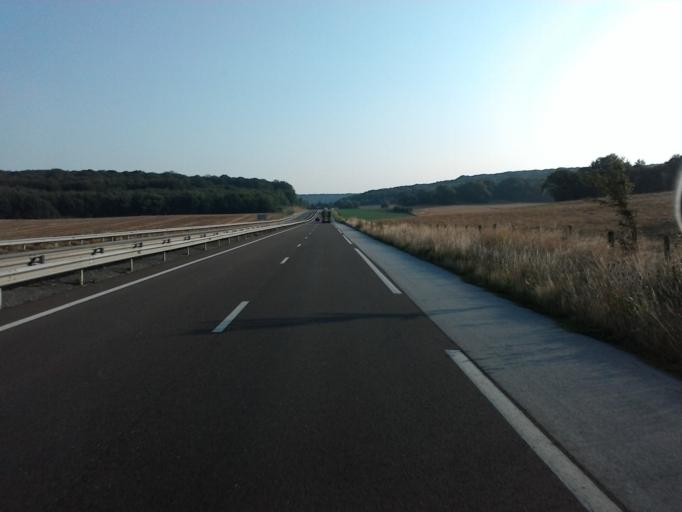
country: FR
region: Franche-Comte
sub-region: Departement de la Haute-Saone
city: Echenoz-la-Meline
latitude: 47.5609
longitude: 6.1376
